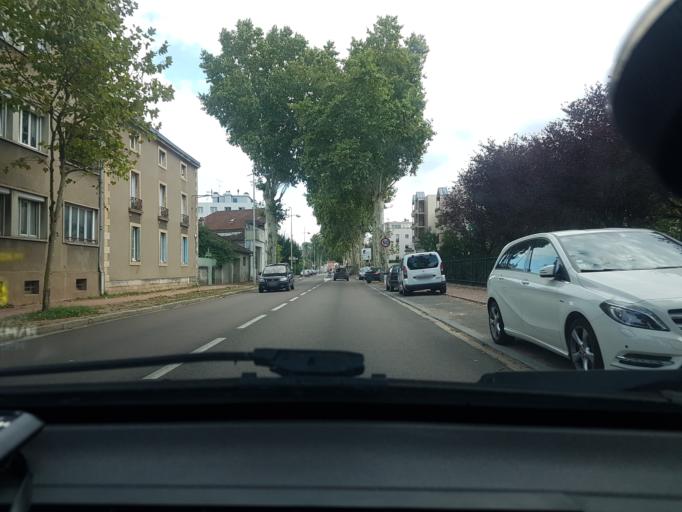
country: FR
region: Bourgogne
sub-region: Departement de la Cote-d'Or
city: Longvic
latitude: 47.3045
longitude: 5.0498
